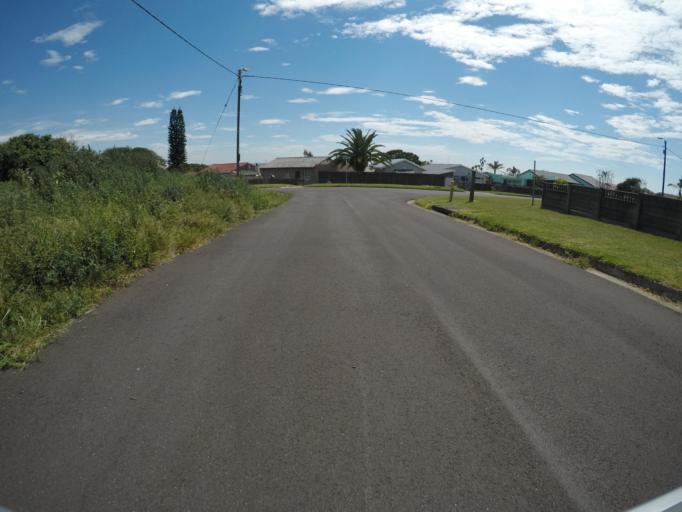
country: ZA
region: Eastern Cape
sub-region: Buffalo City Metropolitan Municipality
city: East London
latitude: -33.0375
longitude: 27.8847
